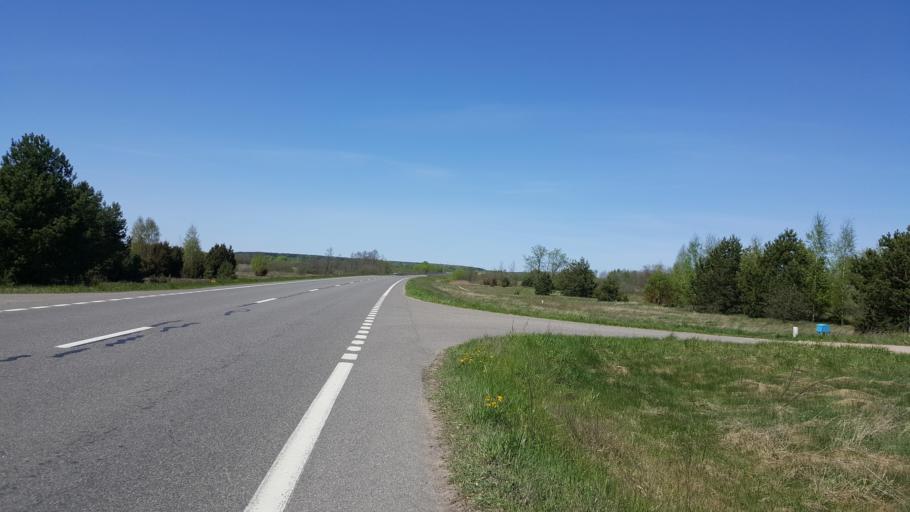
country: BY
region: Brest
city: Kamyanyets
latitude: 52.4236
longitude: 23.8400
